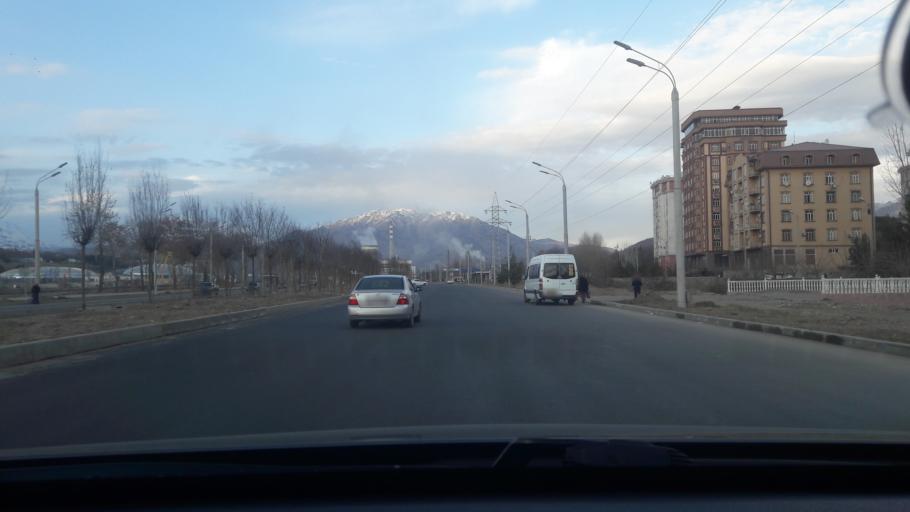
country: TJ
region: Dushanbe
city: Dushanbe
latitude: 38.5919
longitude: 68.7776
